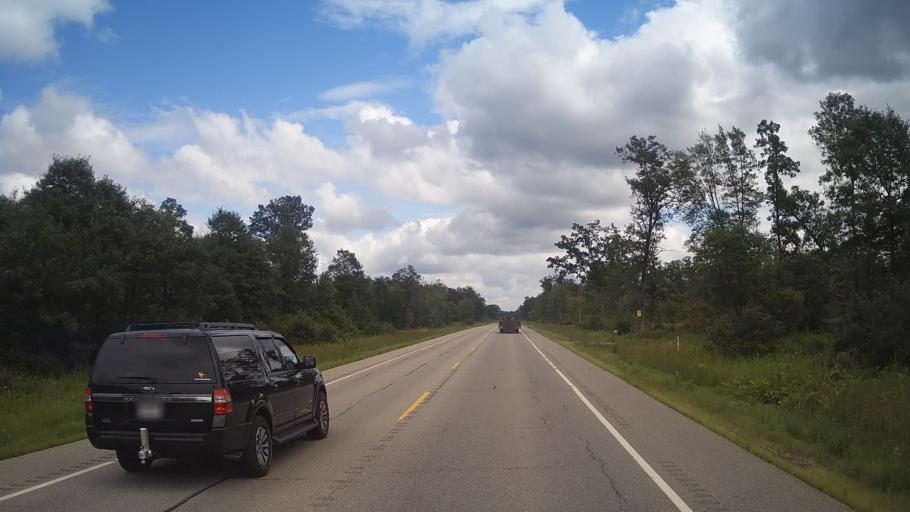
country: US
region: Wisconsin
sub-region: Adams County
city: Friendship
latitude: 44.0256
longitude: -89.7046
